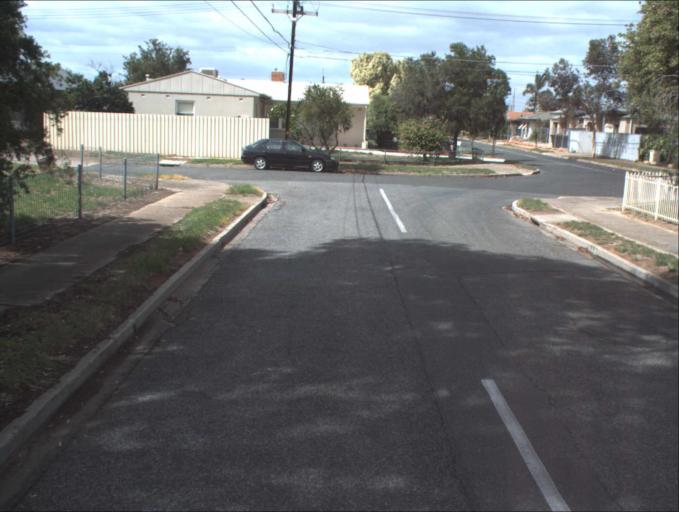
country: AU
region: South Australia
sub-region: Charles Sturt
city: Woodville
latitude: -34.8770
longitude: 138.5628
